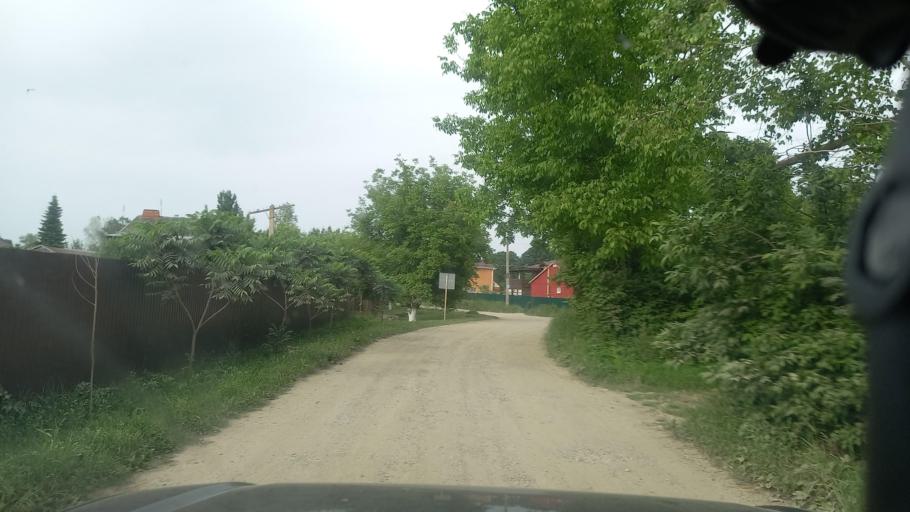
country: RU
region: Krasnodarskiy
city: Saratovskaya
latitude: 44.7515
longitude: 39.2447
